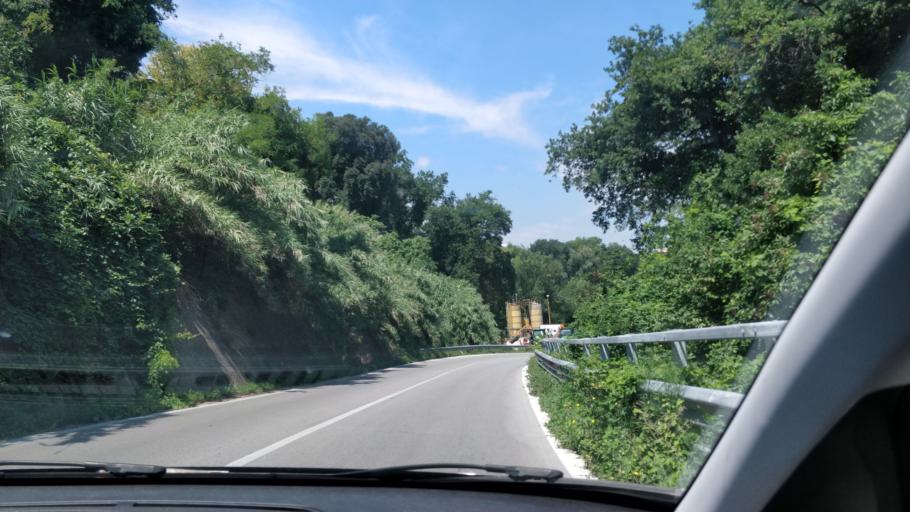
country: IT
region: Abruzzo
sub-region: Provincia di Chieti
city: Ortona
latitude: 42.3376
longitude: 14.4123
